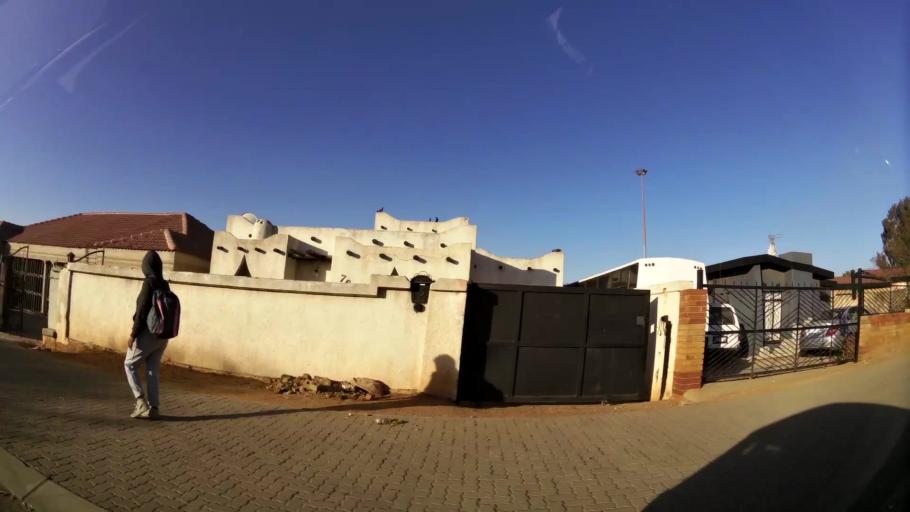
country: ZA
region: Gauteng
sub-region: Ekurhuleni Metropolitan Municipality
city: Tembisa
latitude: -26.0142
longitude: 28.2302
